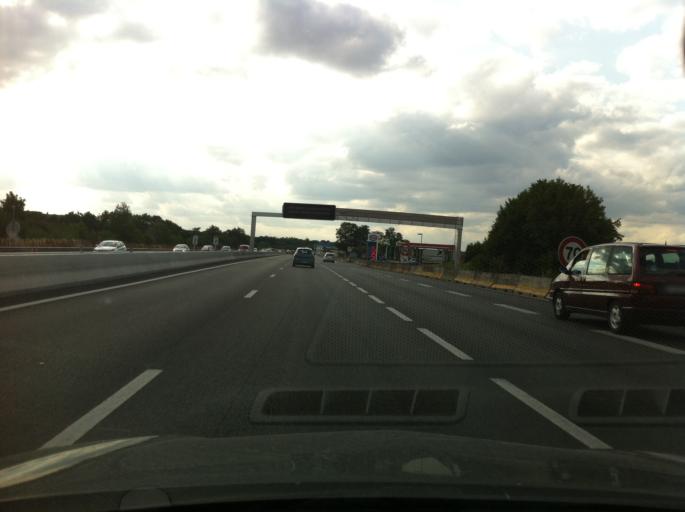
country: FR
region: Ile-de-France
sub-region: Departement de Seine-et-Marne
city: Emerainville
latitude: 48.8152
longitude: 2.6251
